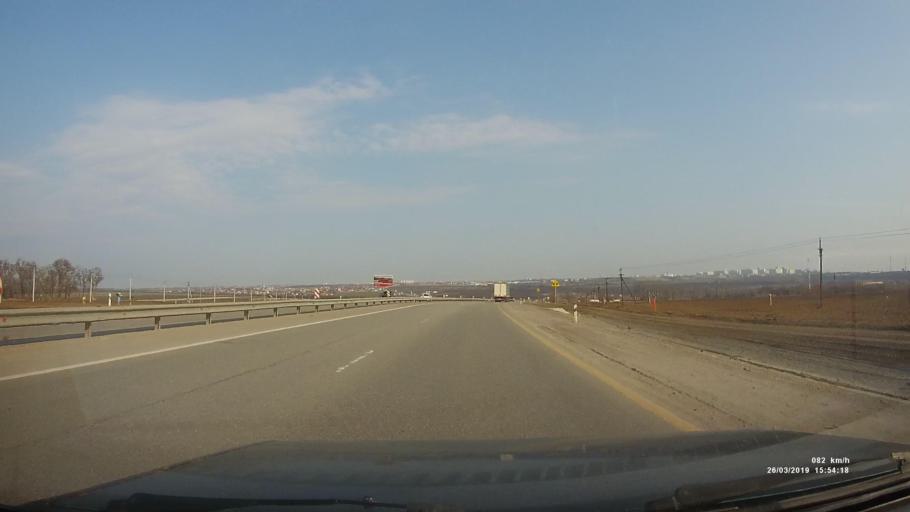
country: RU
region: Rostov
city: Krym
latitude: 47.2703
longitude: 39.5559
